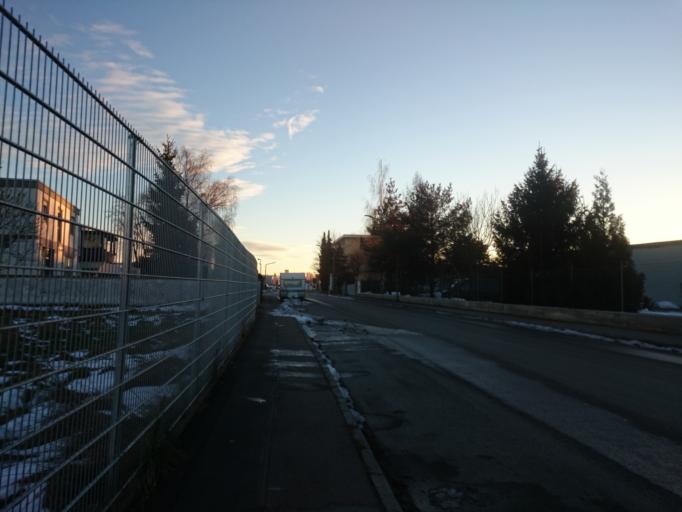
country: DE
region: Bavaria
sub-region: Swabia
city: Konigsbrunn
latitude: 48.2898
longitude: 10.8929
